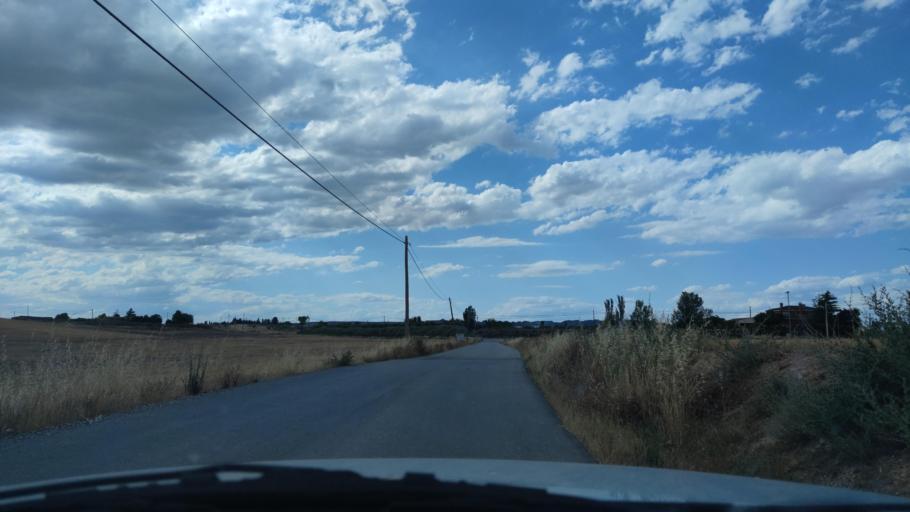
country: ES
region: Catalonia
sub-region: Provincia de Lleida
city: Alcarras
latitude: 41.6054
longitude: 0.5527
